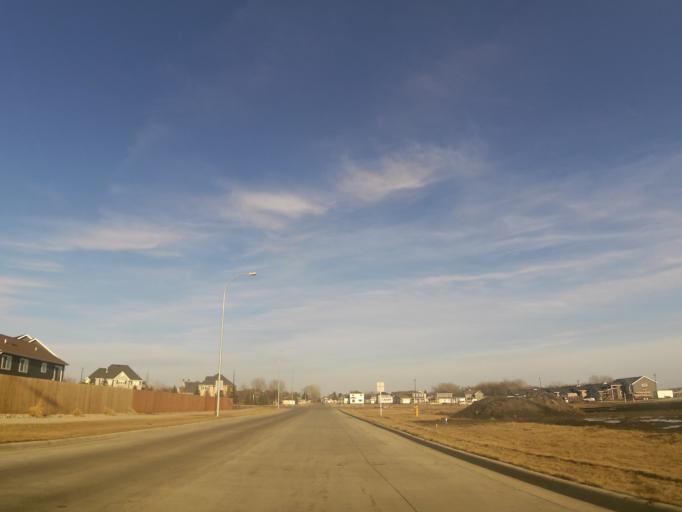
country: US
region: North Dakota
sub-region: Grand Forks County
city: Grand Forks
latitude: 47.8676
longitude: -97.0395
